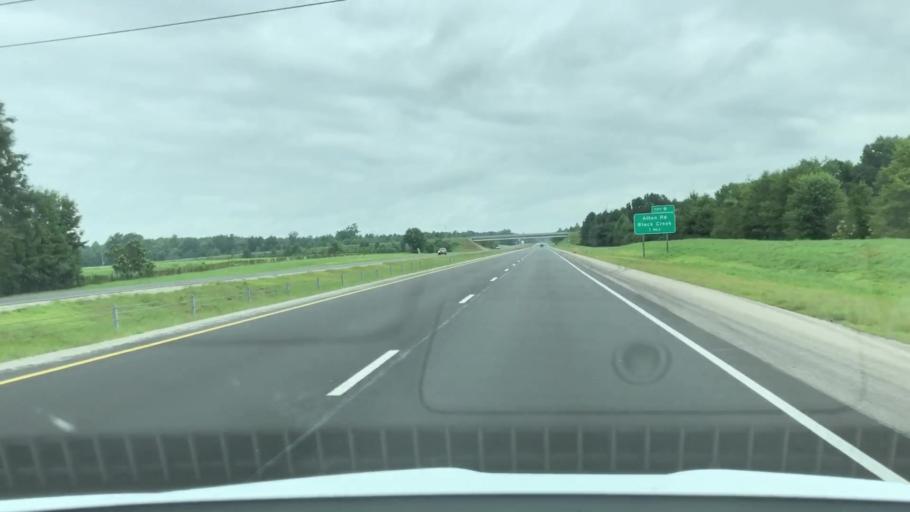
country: US
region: North Carolina
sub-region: Wilson County
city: Lucama
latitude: 35.6007
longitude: -77.9807
